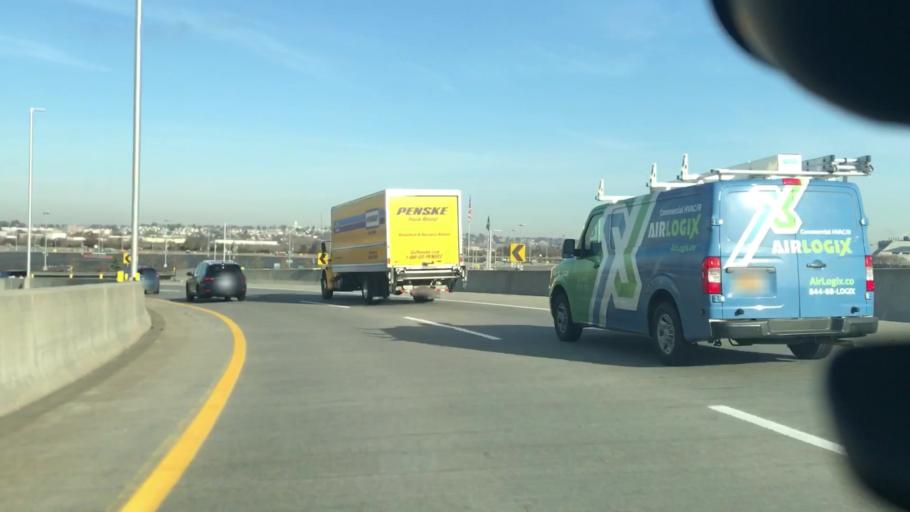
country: US
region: New Jersey
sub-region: Hudson County
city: Secaucus
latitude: 40.8096
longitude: -74.0787
